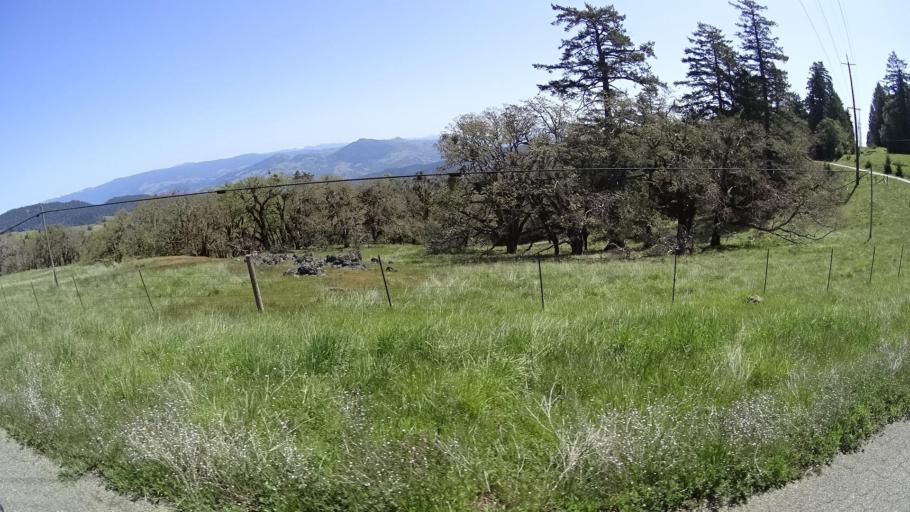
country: US
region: California
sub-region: Humboldt County
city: Redway
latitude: 40.0958
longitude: -123.6816
